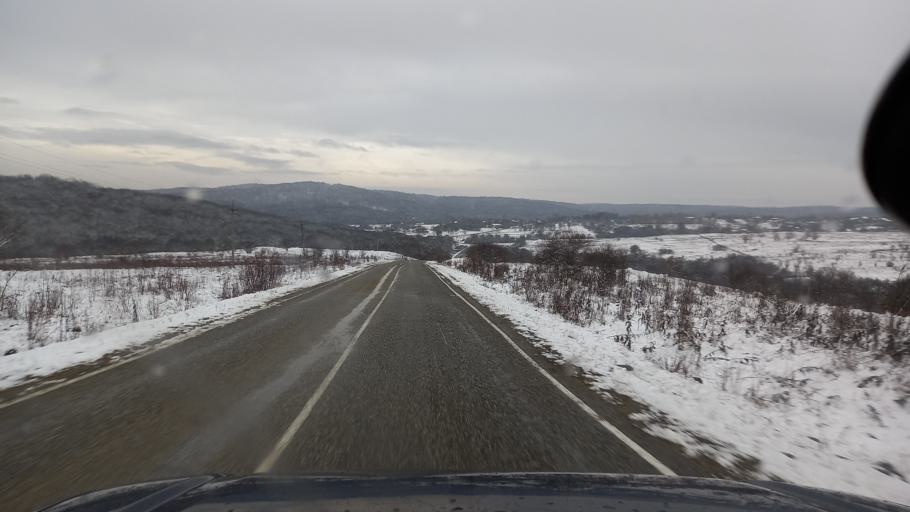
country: RU
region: Adygeya
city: Abadzekhskaya
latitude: 44.3592
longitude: 40.3911
